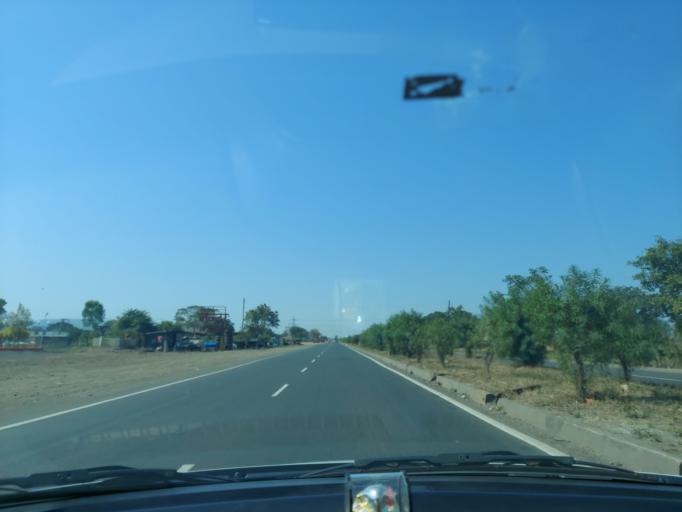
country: IN
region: Madhya Pradesh
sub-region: Indore
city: Manpur
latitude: 22.4217
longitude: 75.6013
